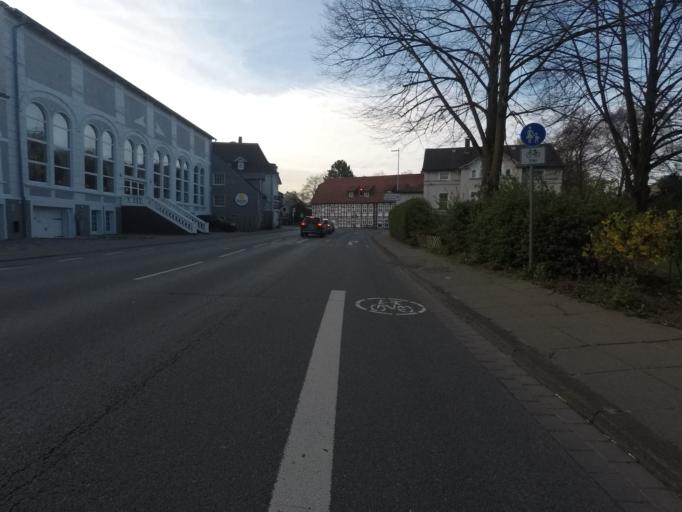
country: DE
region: North Rhine-Westphalia
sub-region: Regierungsbezirk Detmold
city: Bielefeld
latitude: 52.0333
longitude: 8.6032
